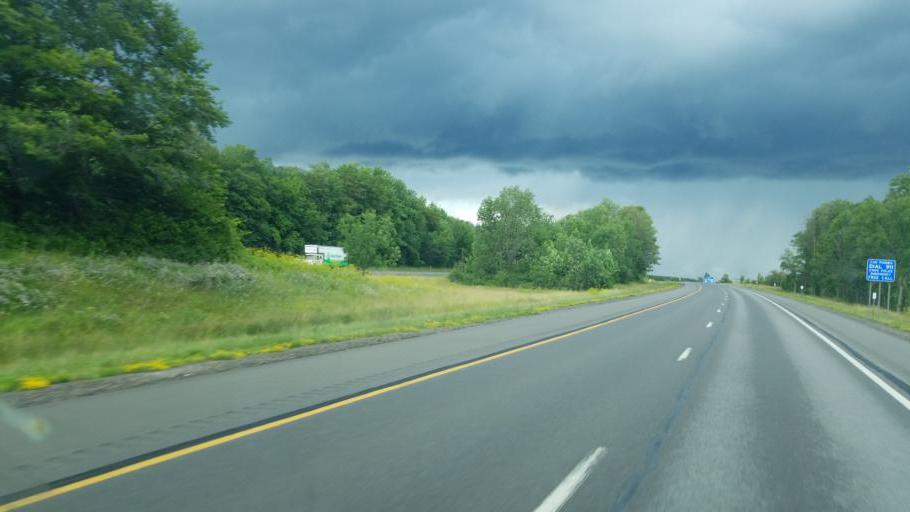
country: US
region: New York
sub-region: Erie County
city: Angola
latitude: 42.6045
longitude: -79.0268
